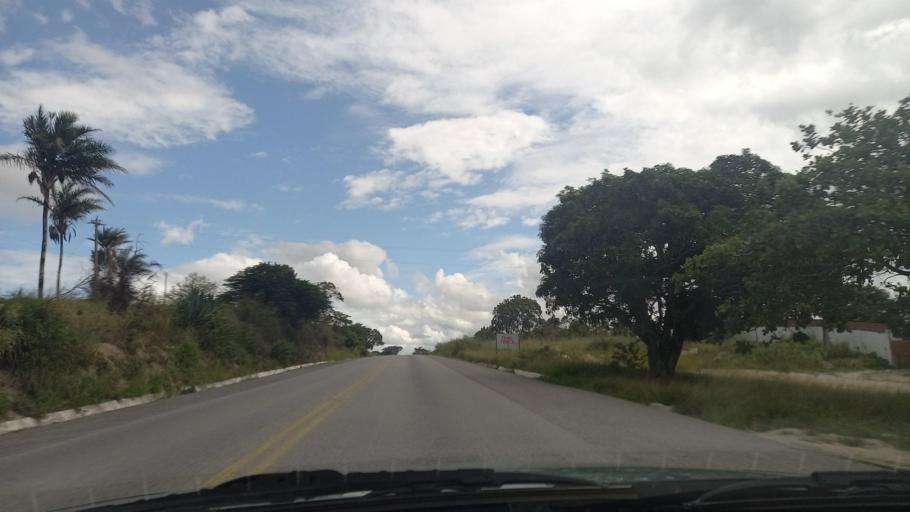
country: BR
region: Pernambuco
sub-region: Lajedo
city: Lajedo
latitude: -8.6776
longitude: -36.4029
